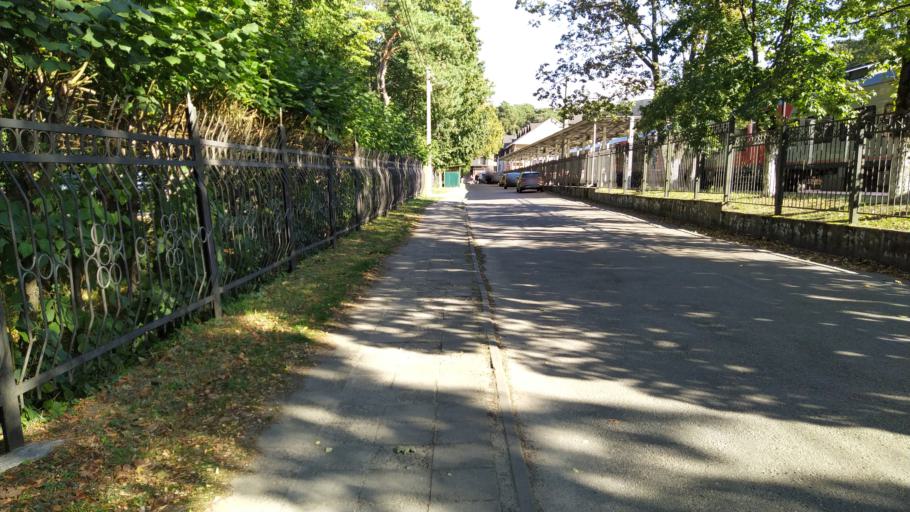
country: RU
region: Kaliningrad
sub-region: Gorod Svetlogorsk
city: Svetlogorsk
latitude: 54.9440
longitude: 20.1449
